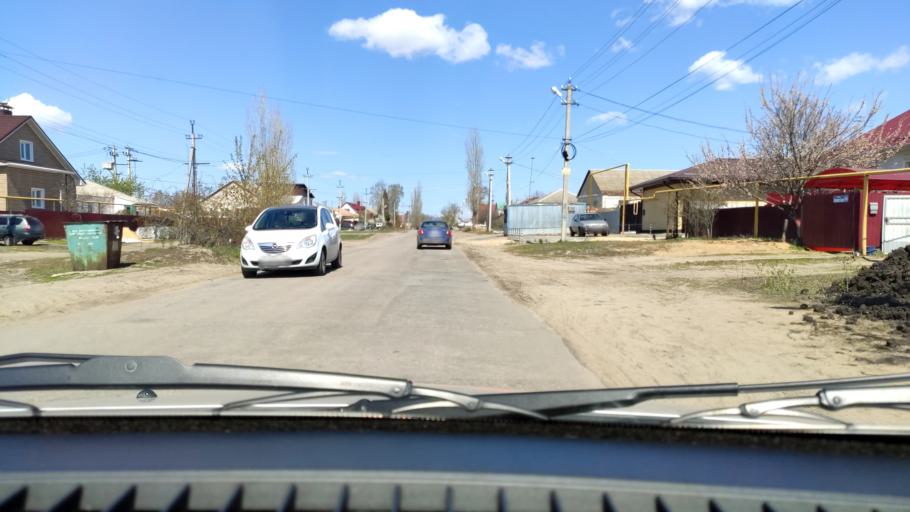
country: RU
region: Voronezj
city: Podgornoye
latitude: 51.7394
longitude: 39.1418
